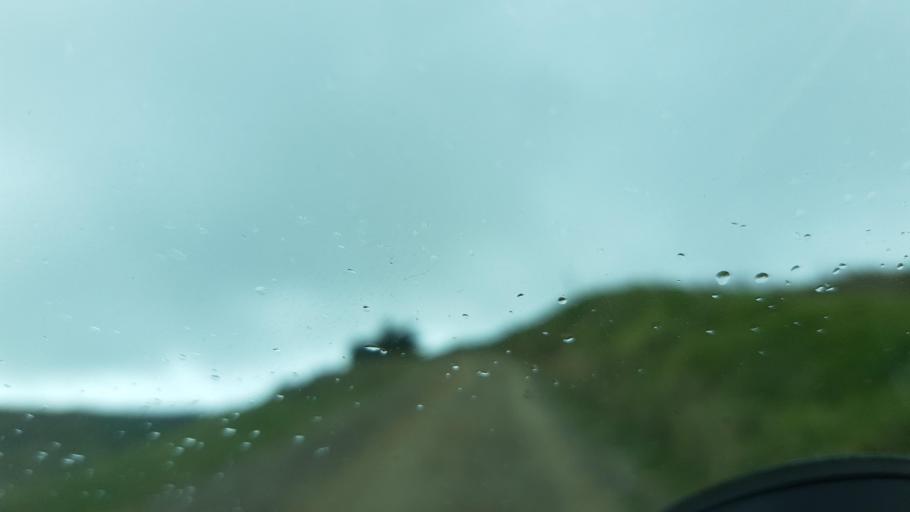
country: CO
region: Boyaca
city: Cucaita
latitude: 5.5170
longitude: -73.4413
